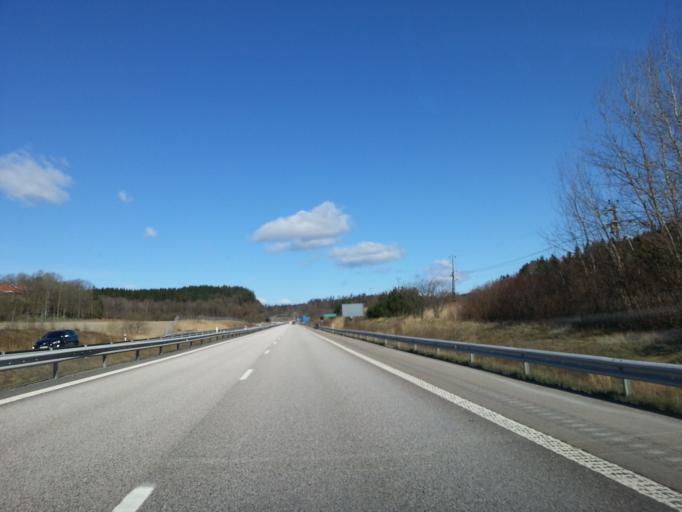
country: SE
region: Vaestra Goetaland
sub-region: Uddevalla Kommun
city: Ljungskile
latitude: 58.2811
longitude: 11.8813
